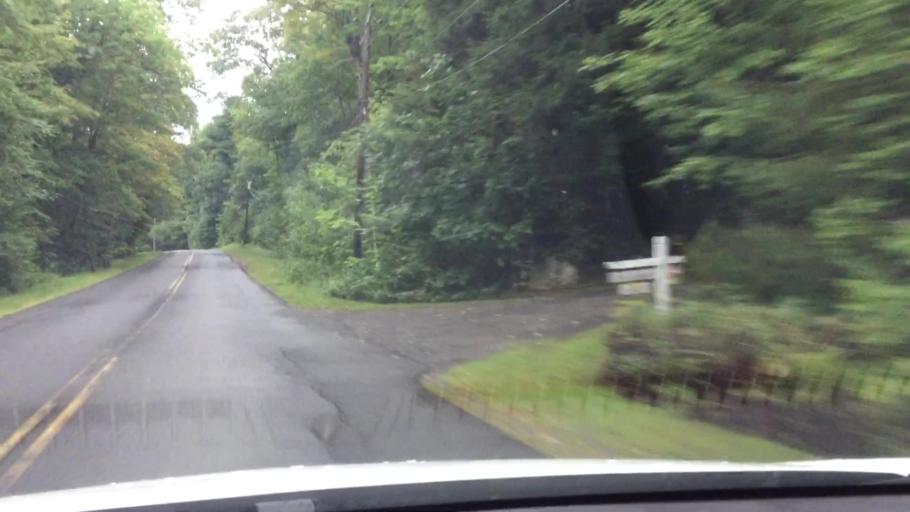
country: US
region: Massachusetts
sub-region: Berkshire County
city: Otis
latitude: 42.1653
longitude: -73.0548
